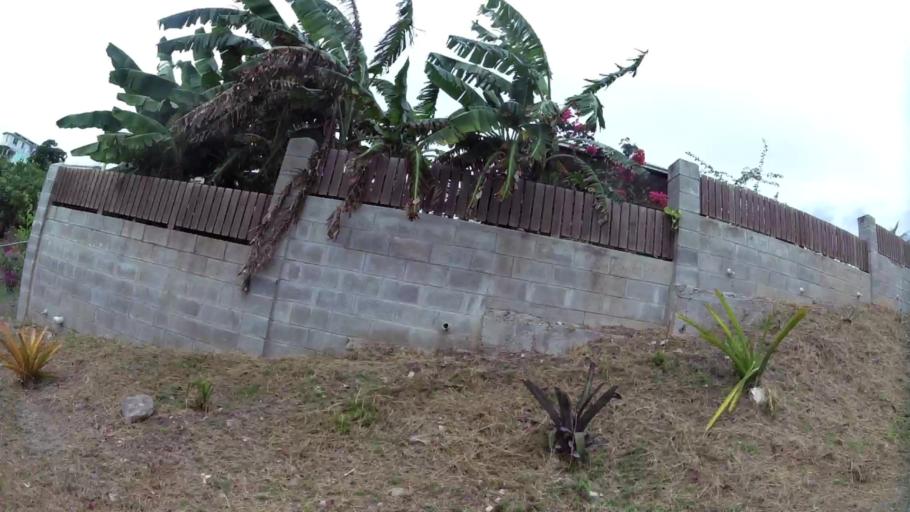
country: AG
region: Saint John
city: Potters Village
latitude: 17.0864
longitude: -61.8075
